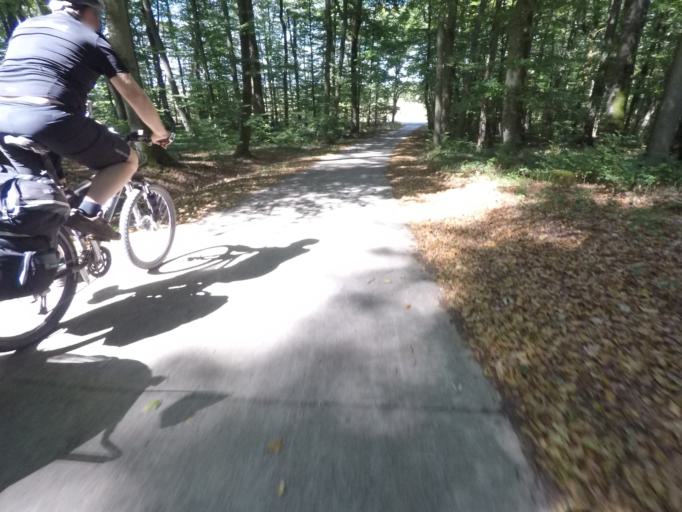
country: LU
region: Luxembourg
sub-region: Canton de Capellen
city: Garnich
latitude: 49.6340
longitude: 5.9432
